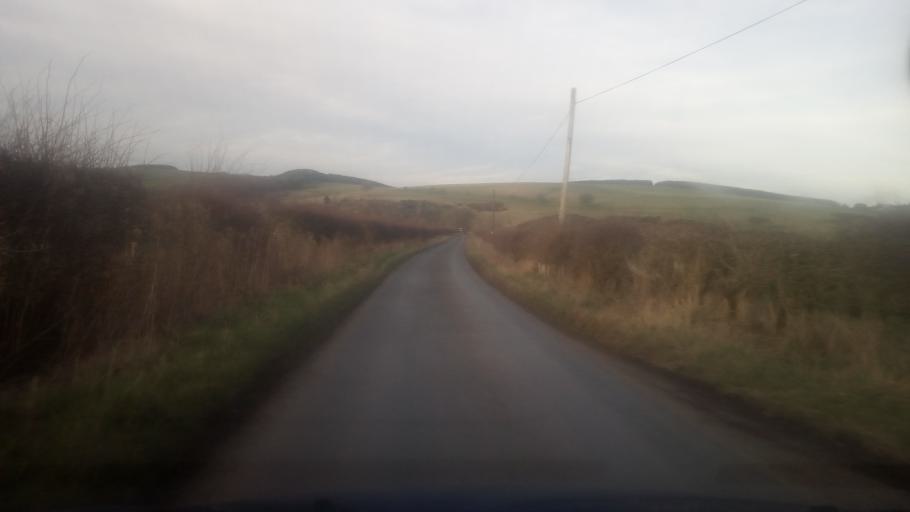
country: GB
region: Scotland
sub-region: The Scottish Borders
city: Jedburgh
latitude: 55.4161
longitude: -2.5153
